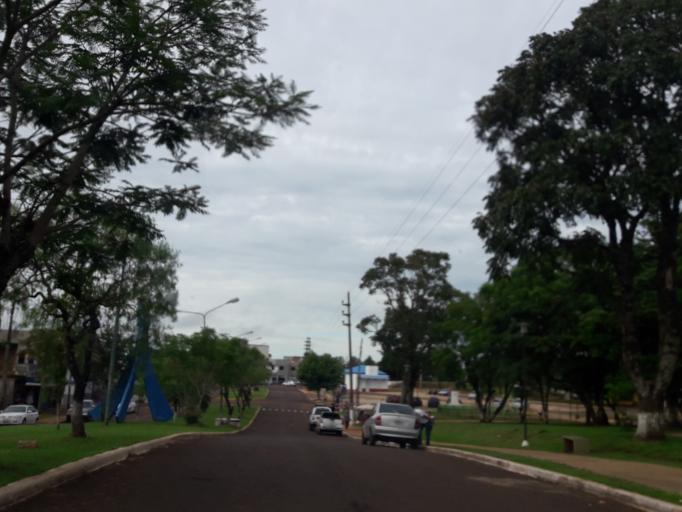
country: AR
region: Misiones
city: Bernardo de Irigoyen
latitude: -26.2555
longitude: -53.6463
